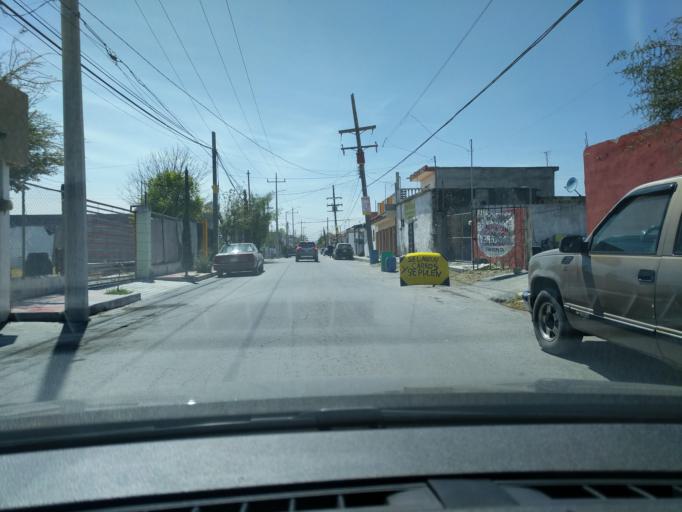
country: MX
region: Nuevo Leon
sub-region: Salinas Victoria
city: Las Torres
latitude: 25.9630
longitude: -100.2982
